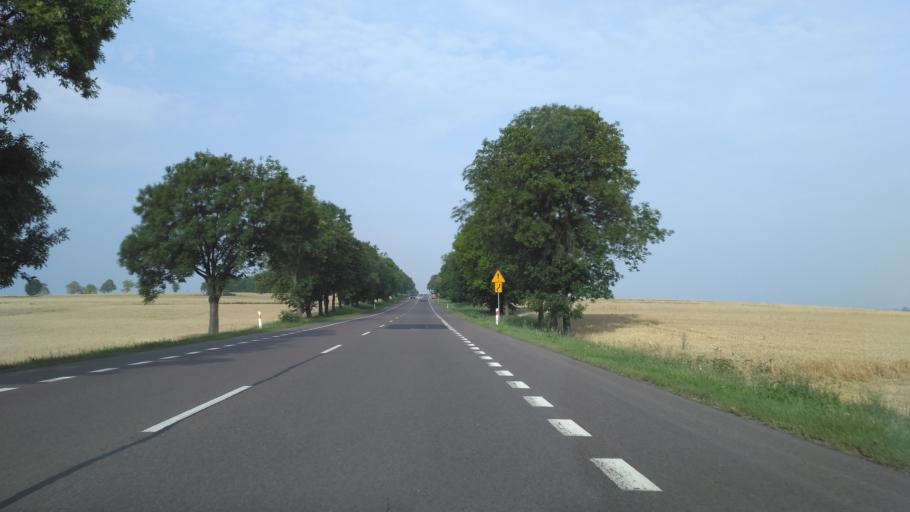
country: PL
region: Lublin Voivodeship
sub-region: Powiat swidnicki
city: Trawniki
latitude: 51.1710
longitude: 23.1194
